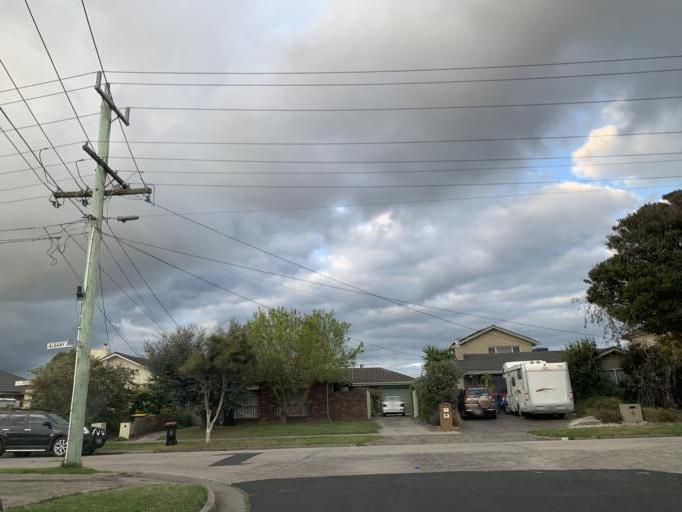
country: AU
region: Victoria
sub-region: Kingston
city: Aspendale
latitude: -38.0250
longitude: 145.1072
